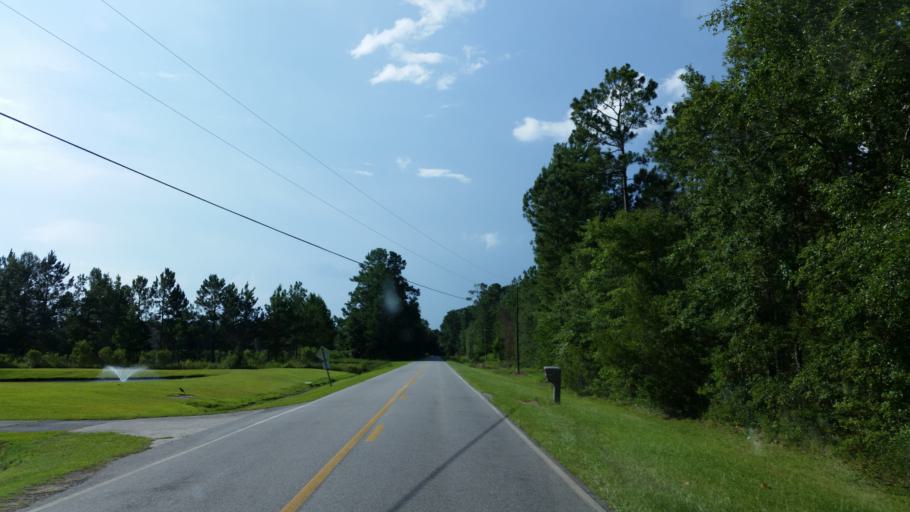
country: US
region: Georgia
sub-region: Lowndes County
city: Hahira
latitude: 30.9427
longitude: -83.4083
